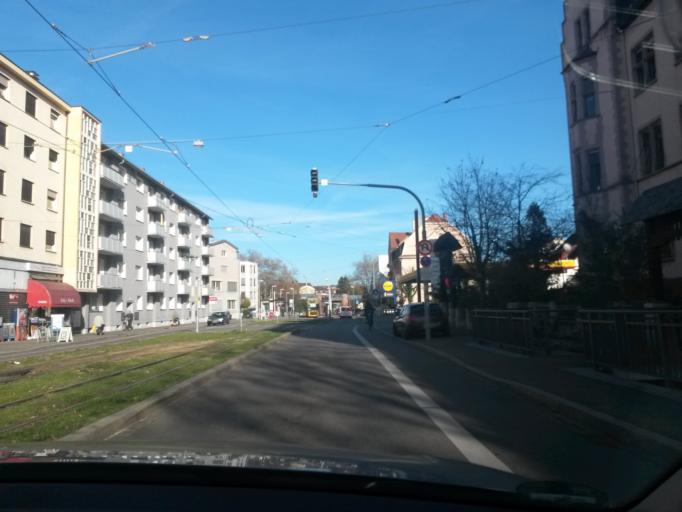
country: DE
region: Baden-Wuerttemberg
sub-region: Freiburg Region
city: Freiburg
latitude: 48.0098
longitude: 7.8547
